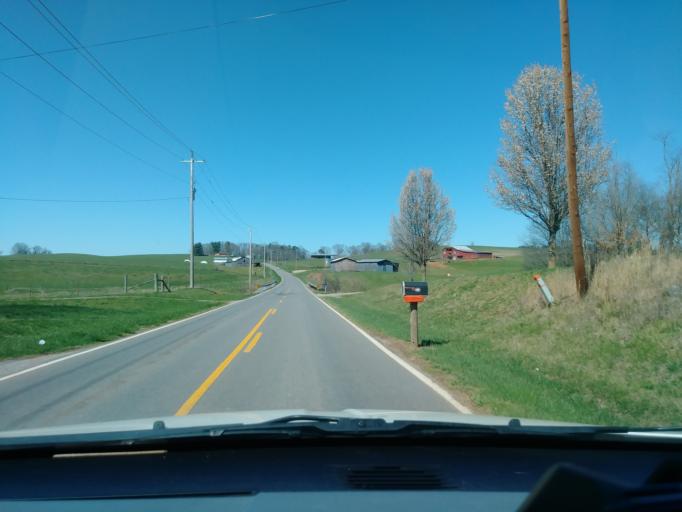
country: US
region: Tennessee
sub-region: Cocke County
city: Newport
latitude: 35.9892
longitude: -83.0653
